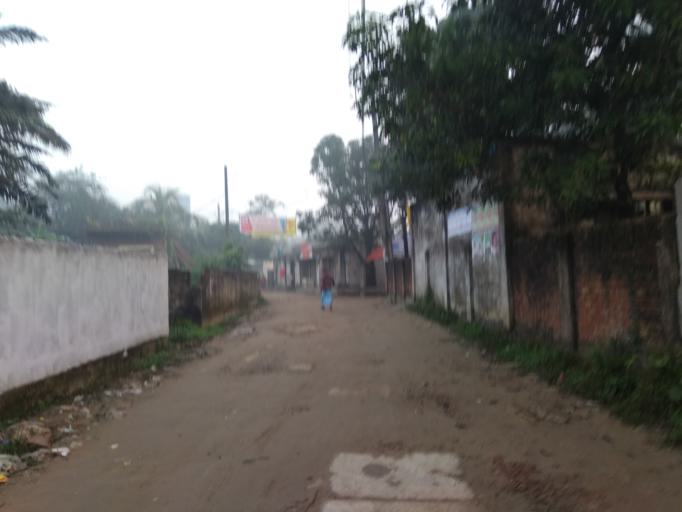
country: BD
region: Dhaka
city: Tungi
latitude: 23.8592
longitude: 90.4329
